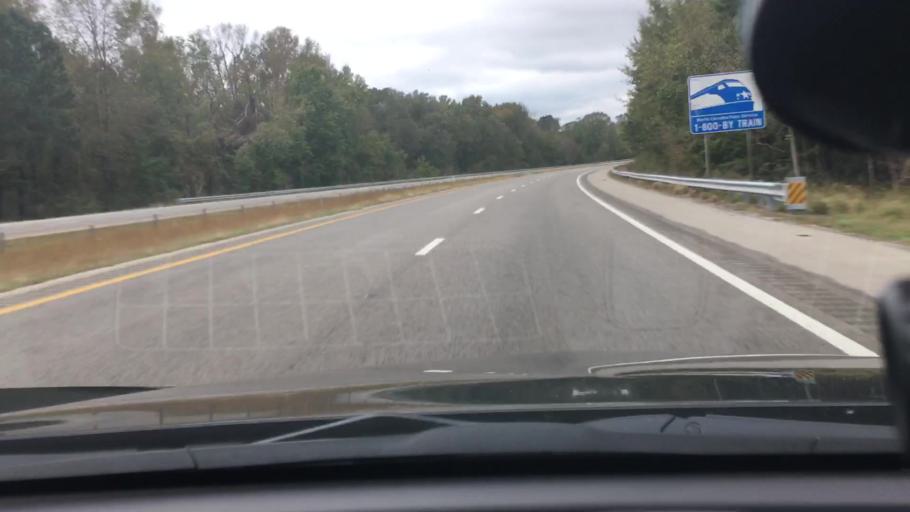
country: US
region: North Carolina
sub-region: Wilson County
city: Wilson
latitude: 35.6688
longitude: -77.8174
